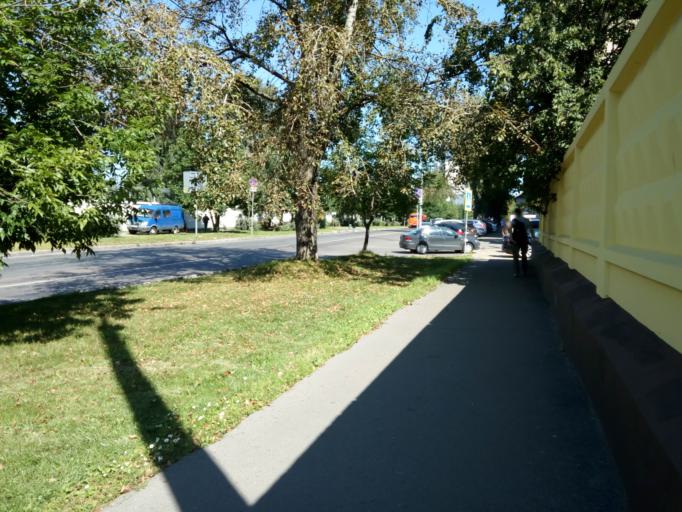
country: RU
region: Moscow
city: Sokol
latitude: 55.7736
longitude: 37.5196
